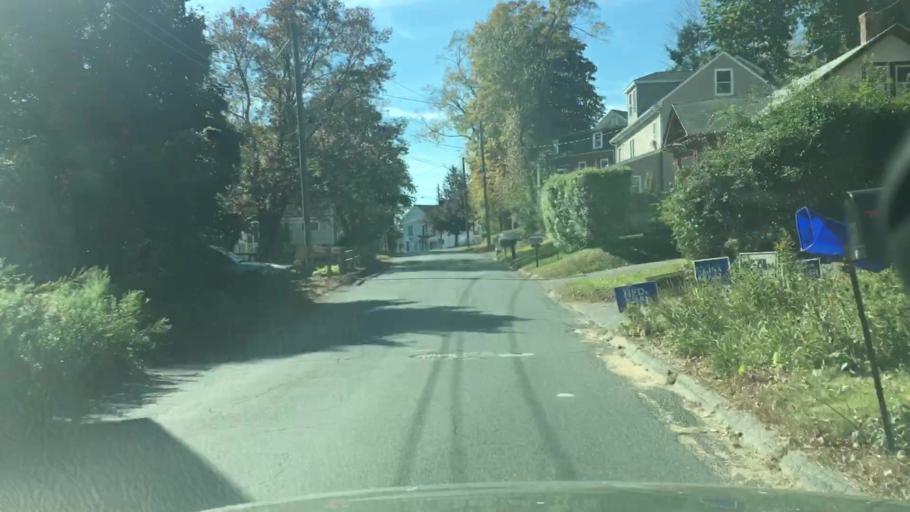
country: US
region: Connecticut
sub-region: Tolland County
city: Stafford
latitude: 41.9885
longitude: -72.2888
